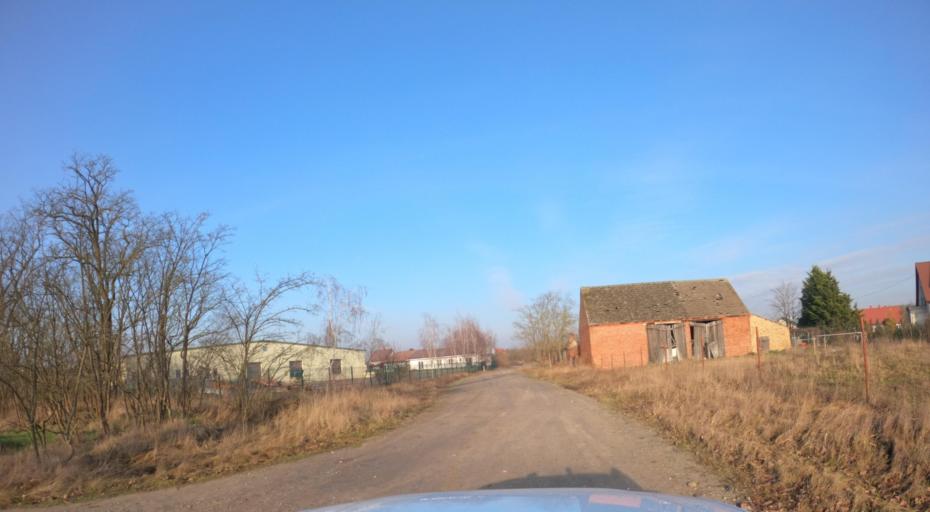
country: PL
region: Lubusz
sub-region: Powiat gorzowski
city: Kostrzyn nad Odra
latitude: 52.6202
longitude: 14.5870
